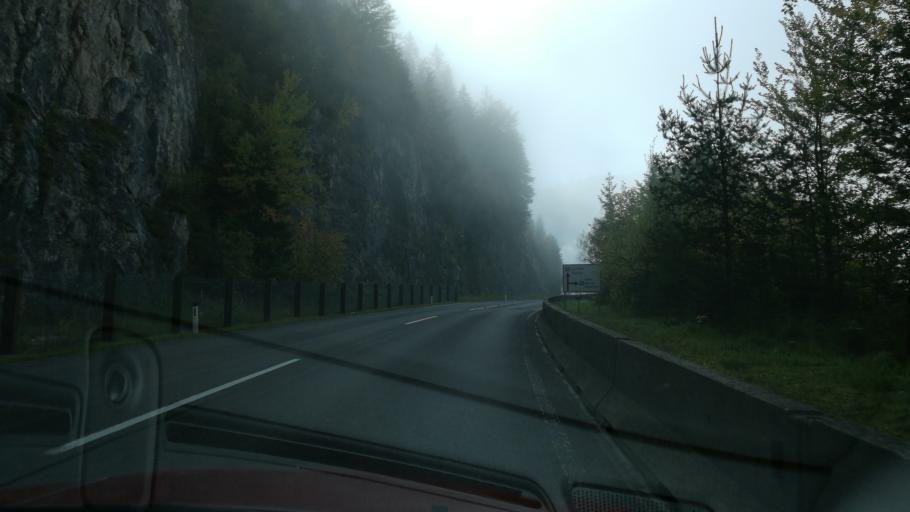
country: AT
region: Styria
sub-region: Politischer Bezirk Liezen
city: Altenmarkt bei Sankt Gallen
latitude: 47.7269
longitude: 14.6501
